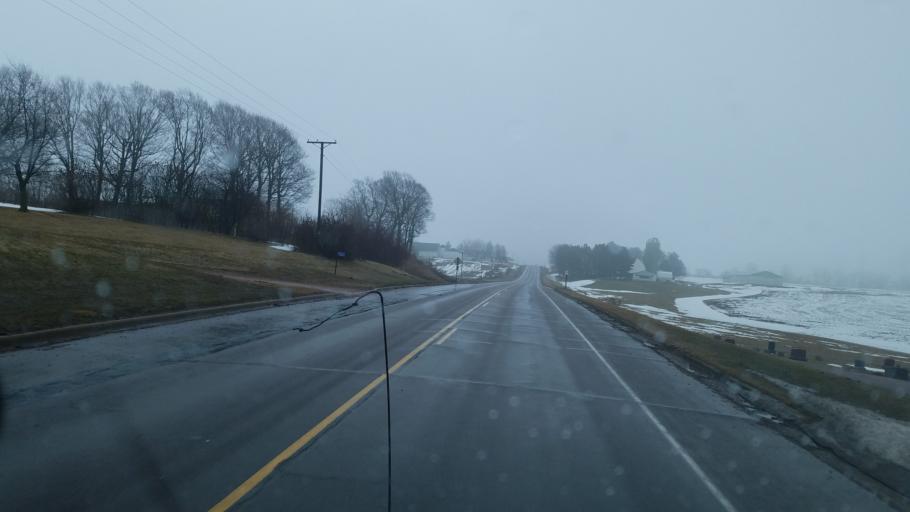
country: US
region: Wisconsin
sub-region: Wood County
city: Marshfield
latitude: 44.5989
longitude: -90.2768
